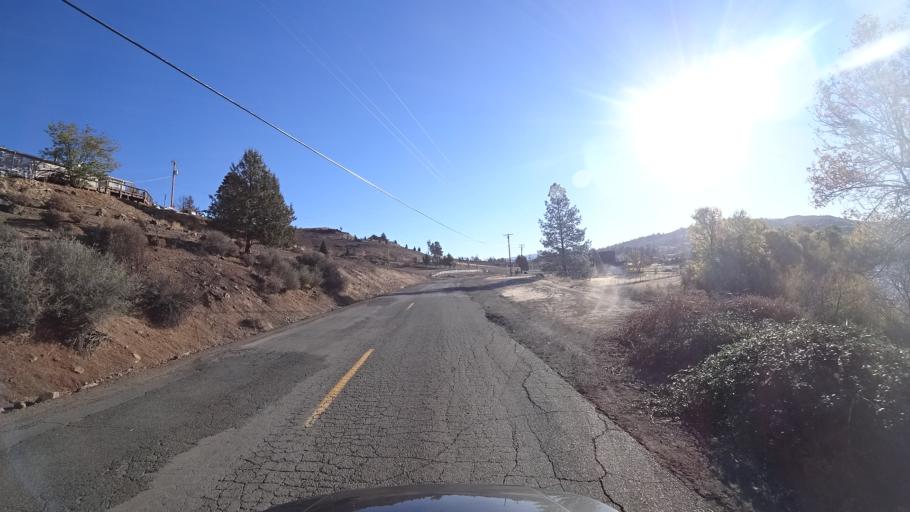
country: US
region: California
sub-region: Siskiyou County
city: Montague
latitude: 41.9005
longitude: -122.4909
